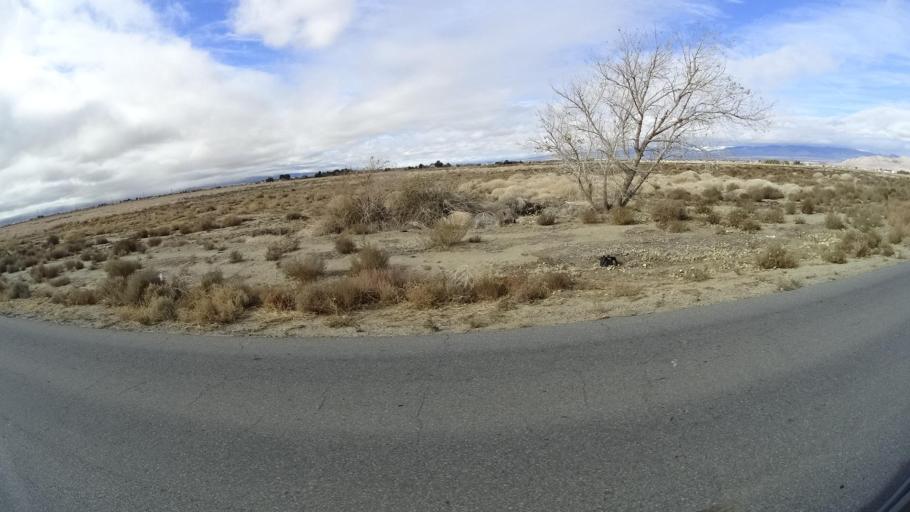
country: US
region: California
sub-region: Kern County
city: Rosamond
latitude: 34.8237
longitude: -118.2377
